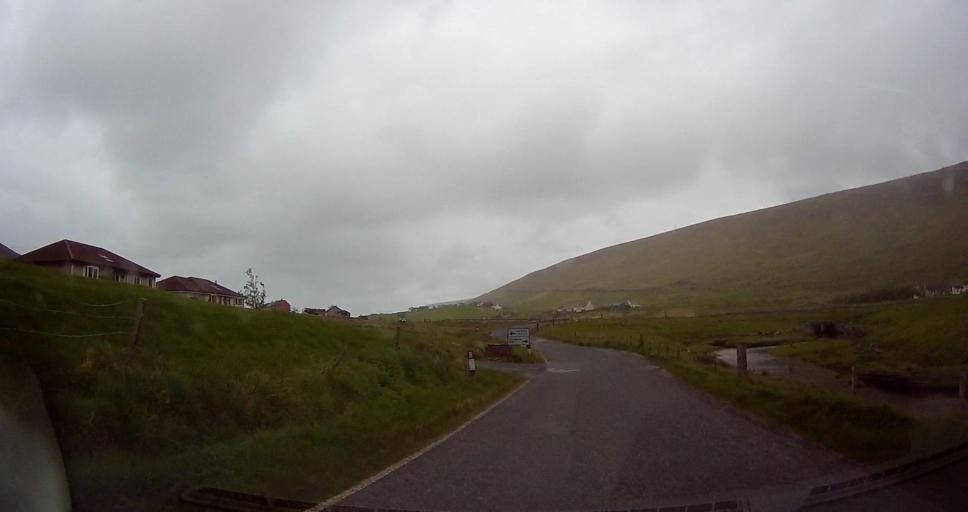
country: GB
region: Scotland
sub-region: Shetland Islands
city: Lerwick
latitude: 60.2544
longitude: -1.2898
